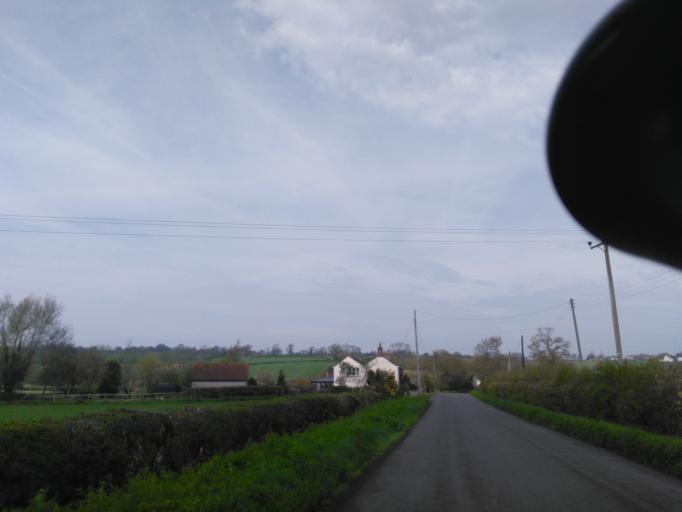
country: GB
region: England
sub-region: Somerset
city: Langport
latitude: 51.1208
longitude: -2.8245
